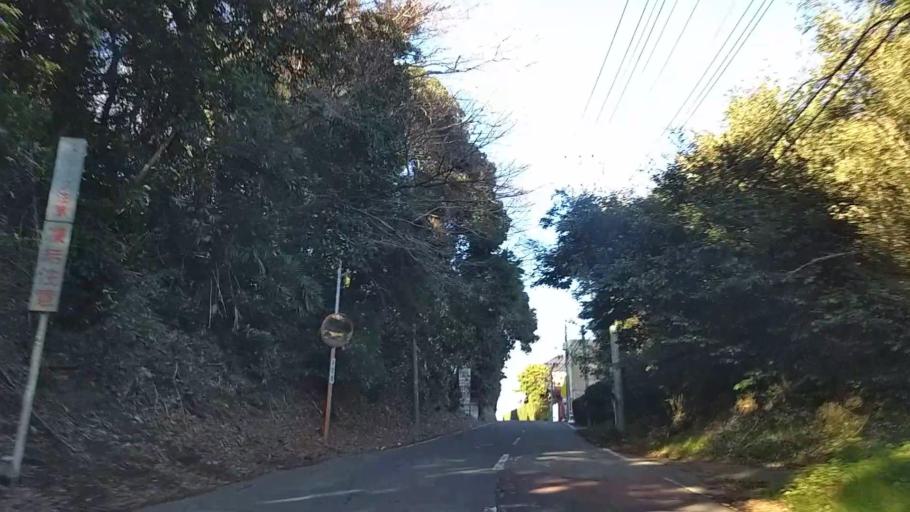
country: JP
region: Chiba
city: Asahi
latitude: 35.7210
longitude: 140.7349
